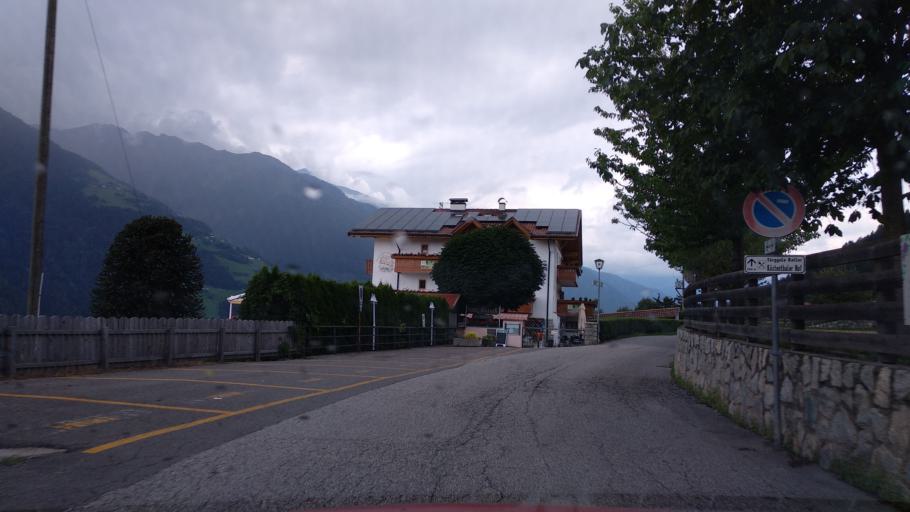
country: IT
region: Trentino-Alto Adige
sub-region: Bolzano
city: Scena
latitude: 46.6988
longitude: 11.2021
